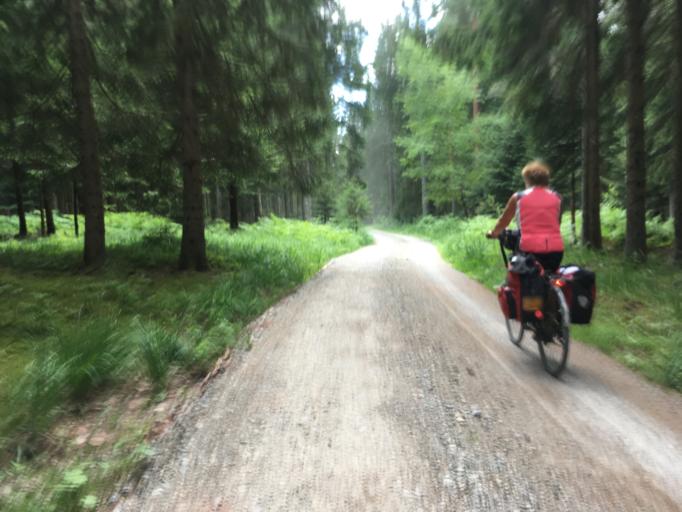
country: DE
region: Baden-Wuerttemberg
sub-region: Karlsruhe Region
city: Baiersbronn
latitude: 48.5497
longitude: 8.4190
